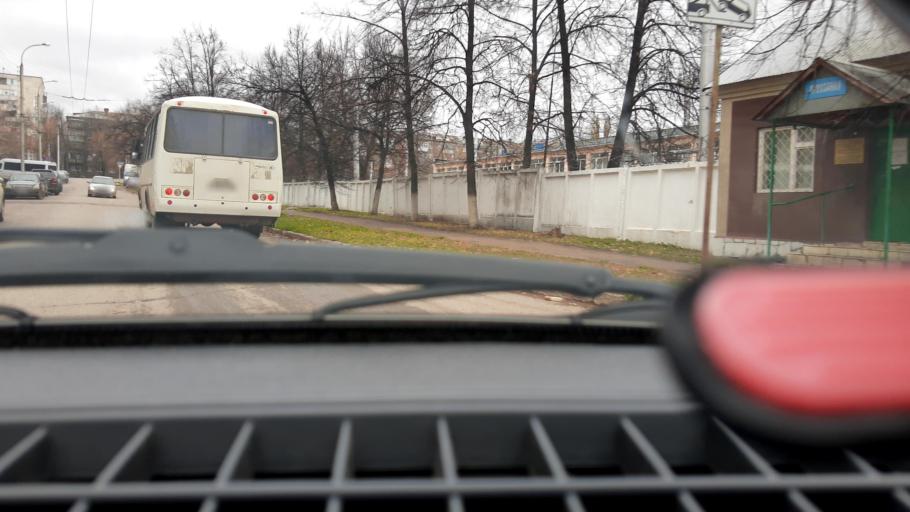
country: RU
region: Bashkortostan
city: Ufa
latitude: 54.8154
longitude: 56.1290
